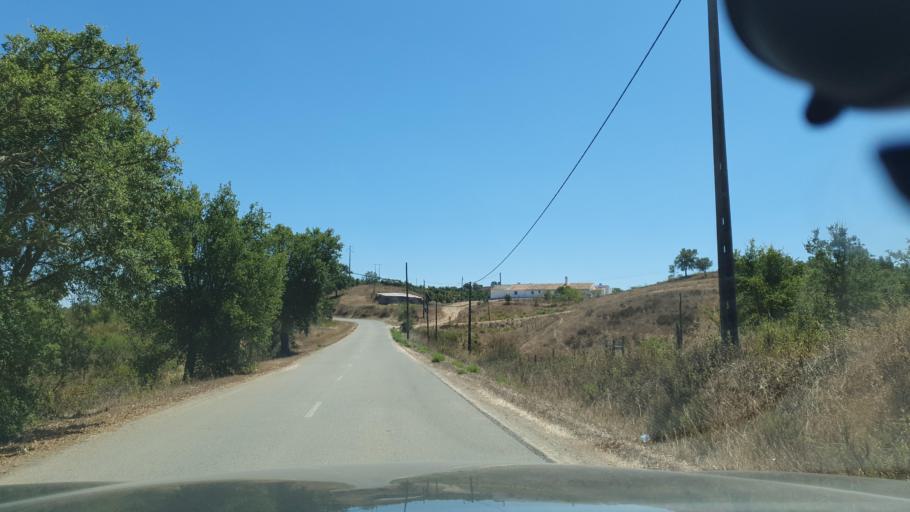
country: PT
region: Beja
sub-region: Odemira
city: Odemira
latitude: 37.5507
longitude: -8.4246
